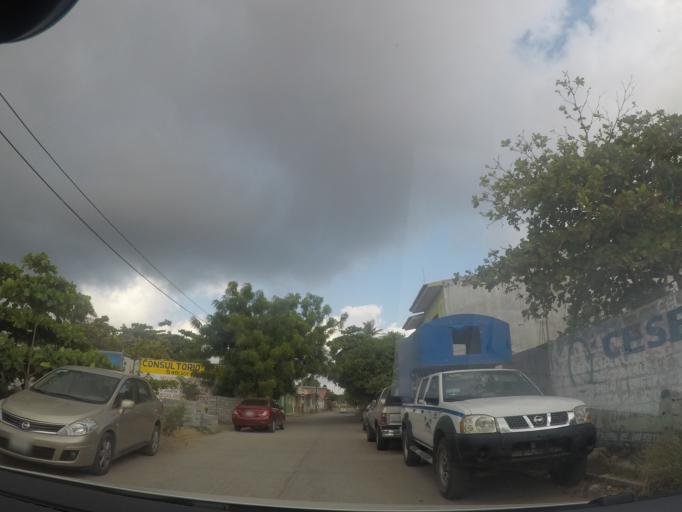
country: MX
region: Oaxaca
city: Juchitan de Zaragoza
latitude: 16.4334
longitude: -95.0323
